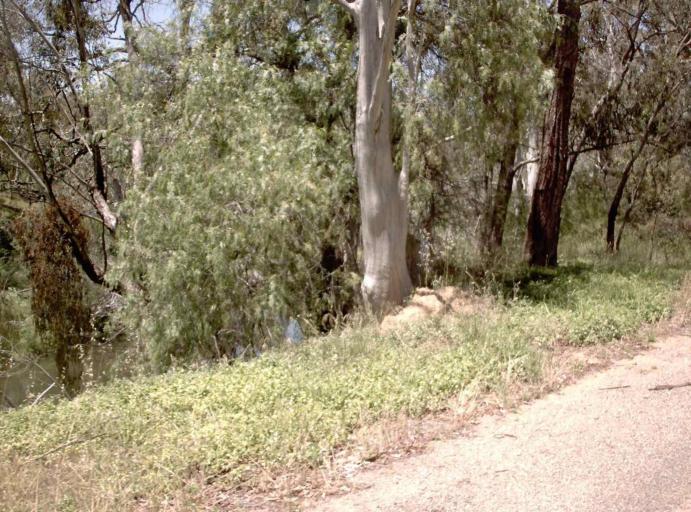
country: AU
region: Victoria
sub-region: East Gippsland
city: Bairnsdale
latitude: -37.4121
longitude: 147.8347
